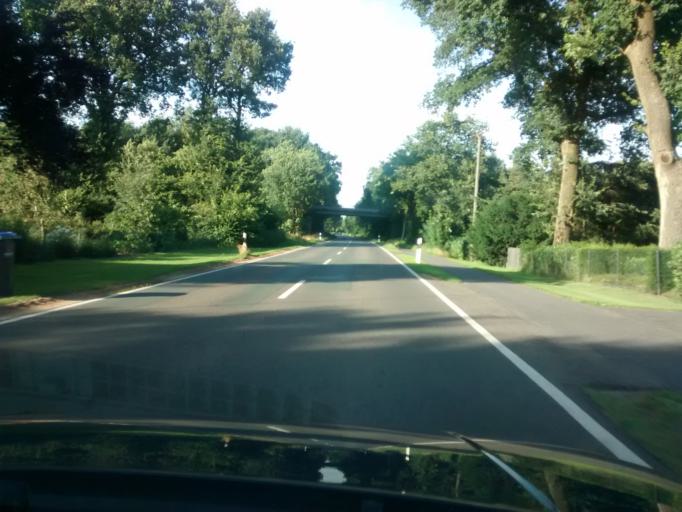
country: DE
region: Lower Saxony
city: Meppen
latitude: 52.6767
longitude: 7.2374
